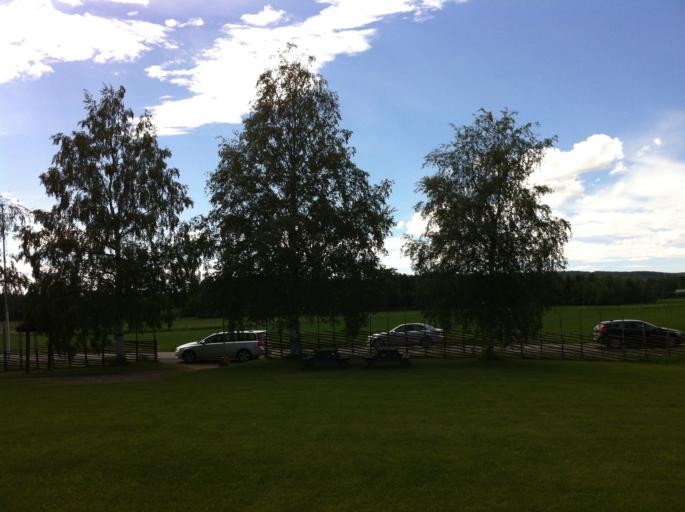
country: SE
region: Gaevleborg
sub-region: Ovanakers Kommun
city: Alfta
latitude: 61.3598
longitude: 16.0500
